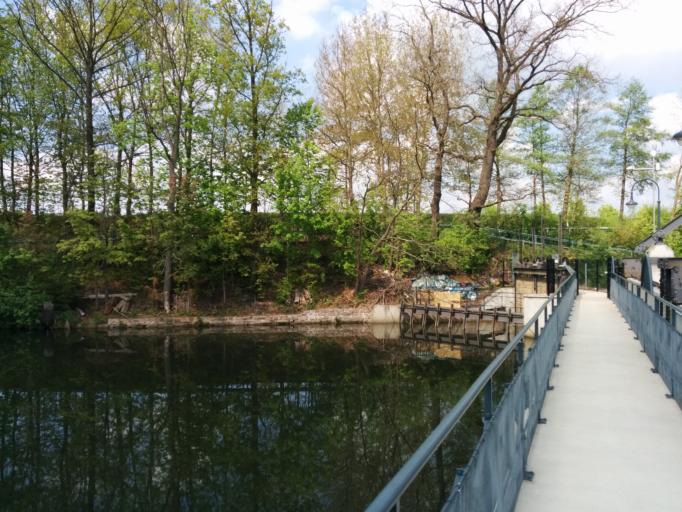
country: DE
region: Saxony
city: Floha
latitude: 50.8429
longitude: 13.0774
